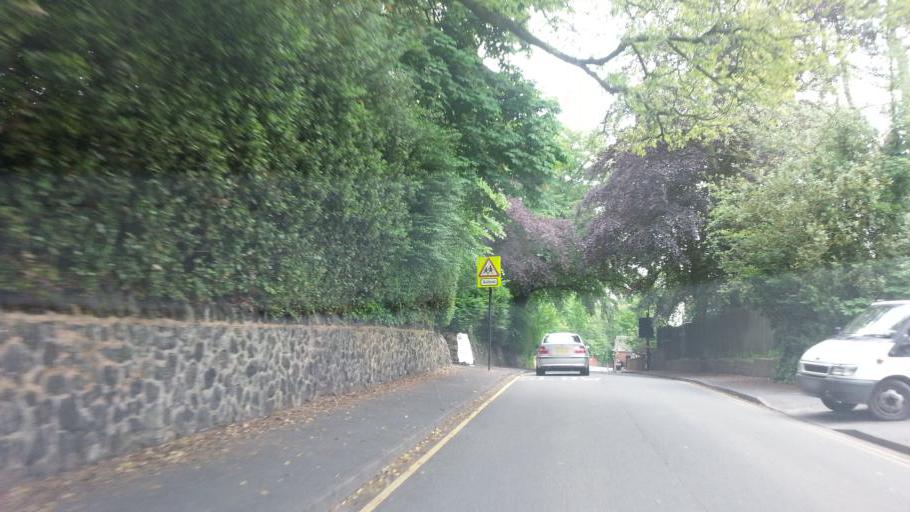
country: GB
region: England
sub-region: City and Borough of Birmingham
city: Birmingham
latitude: 52.4682
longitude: -1.9129
